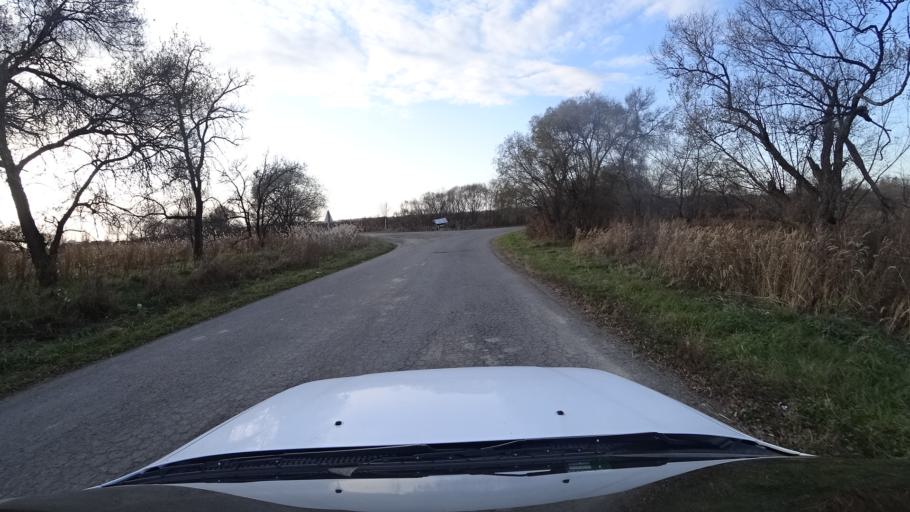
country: RU
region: Primorskiy
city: Lazo
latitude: 45.8243
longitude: 133.6134
